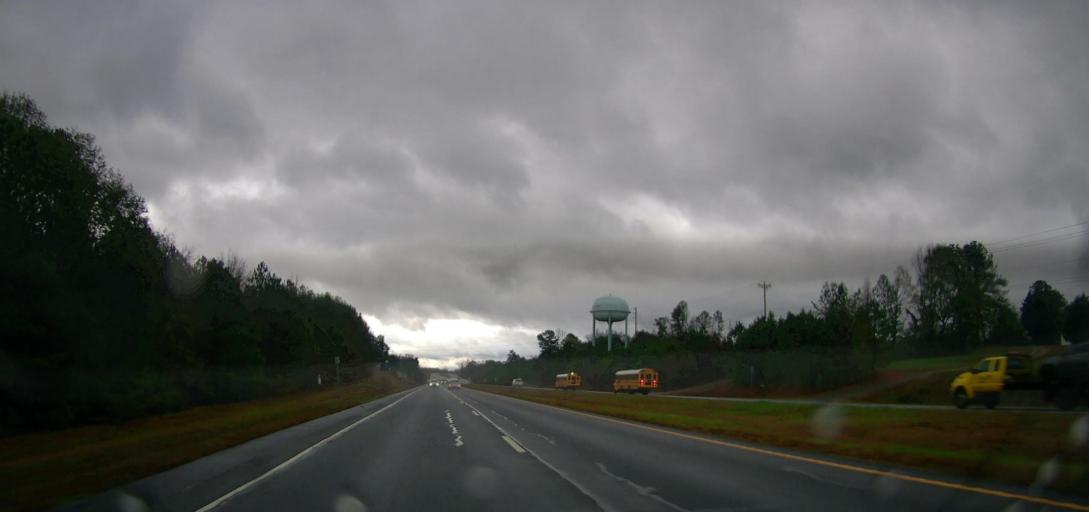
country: US
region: Georgia
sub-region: Jackson County
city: Nicholson
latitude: 34.1421
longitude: -83.4345
